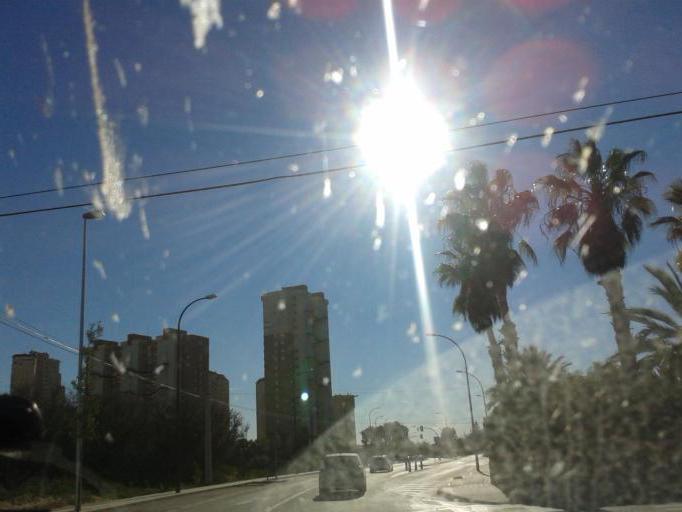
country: ES
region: Valencia
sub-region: Provincia de Alicante
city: el Campello
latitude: 38.4098
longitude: -0.4073
